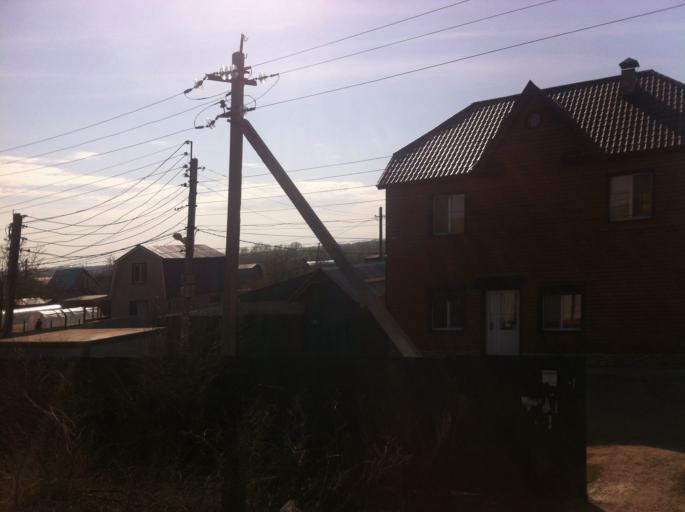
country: RU
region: Samara
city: Smyshlyayevka
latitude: 53.1157
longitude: 50.4143
